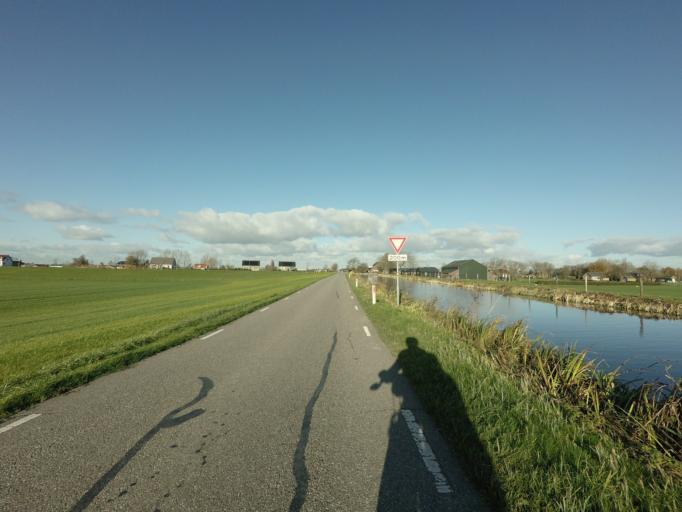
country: NL
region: South Holland
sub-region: Gemeente Nieuwkoop
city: Nieuwkoop
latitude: 52.2024
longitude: 4.7693
